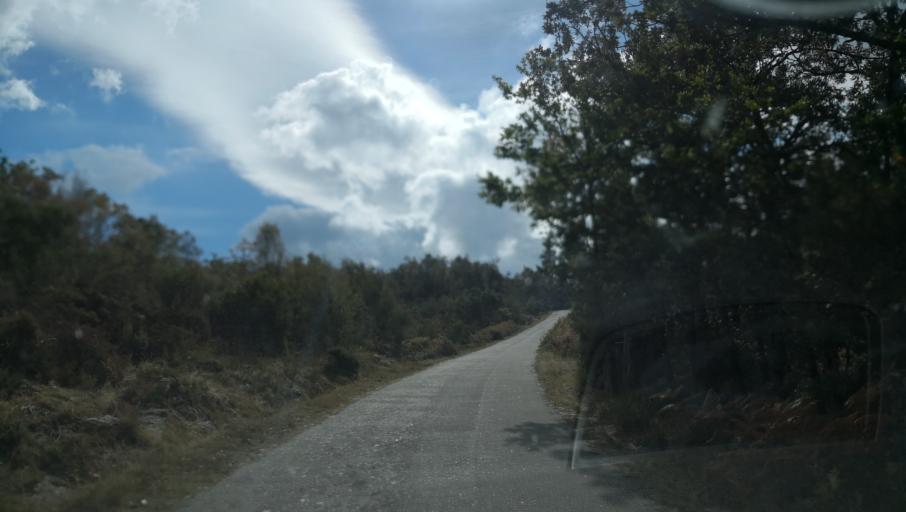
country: PT
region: Vila Real
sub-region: Vila Real
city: Vila Real
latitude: 41.3649
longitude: -7.7932
